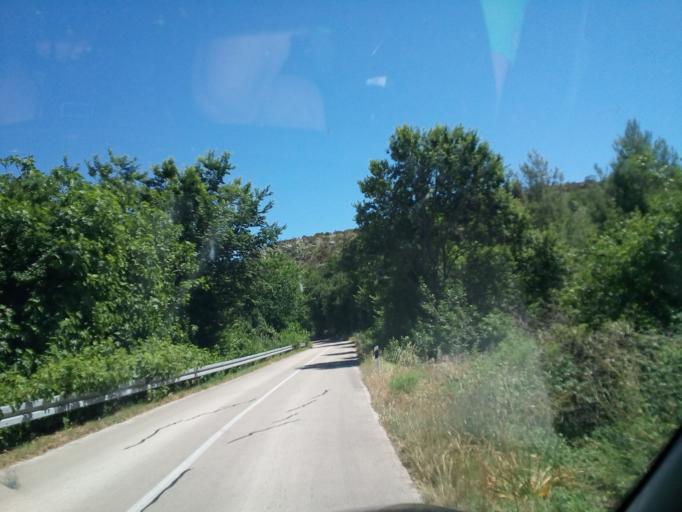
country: HR
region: Zadarska
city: Posedarje
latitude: 44.2034
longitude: 15.4720
